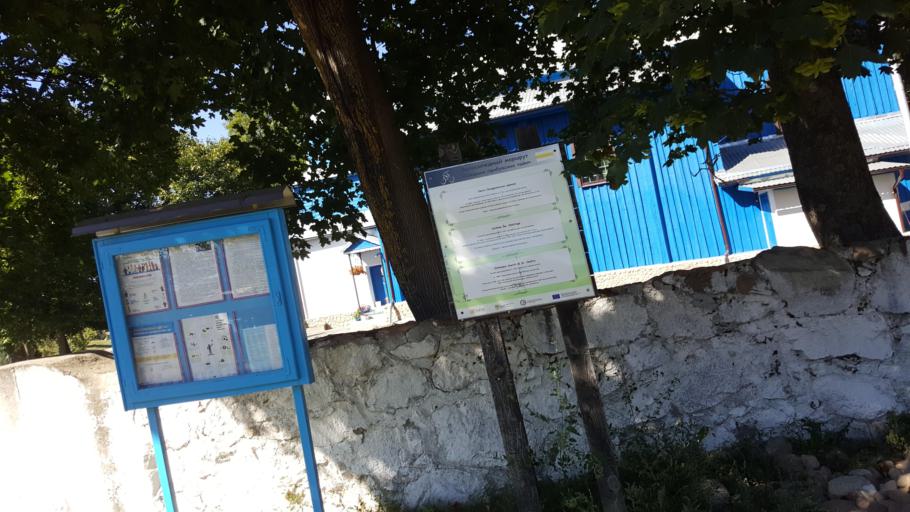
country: PL
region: Lublin Voivodeship
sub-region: Powiat bialski
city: Rokitno
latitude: 52.2234
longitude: 23.3432
